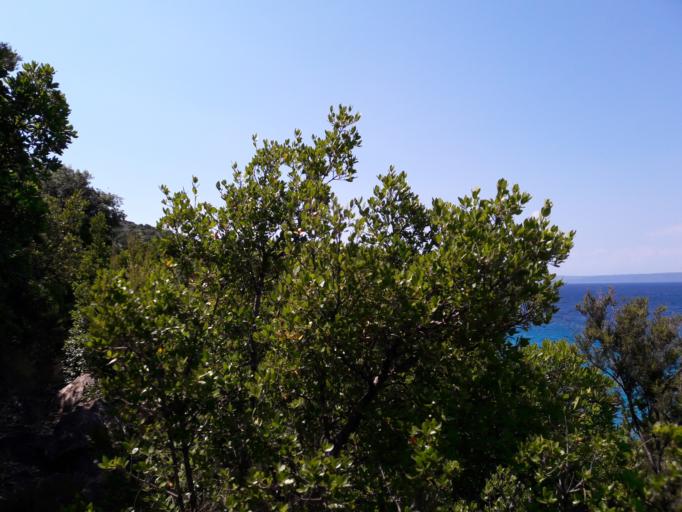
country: HR
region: Dubrovacko-Neretvanska
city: Orebic
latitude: 43.0232
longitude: 17.1594
